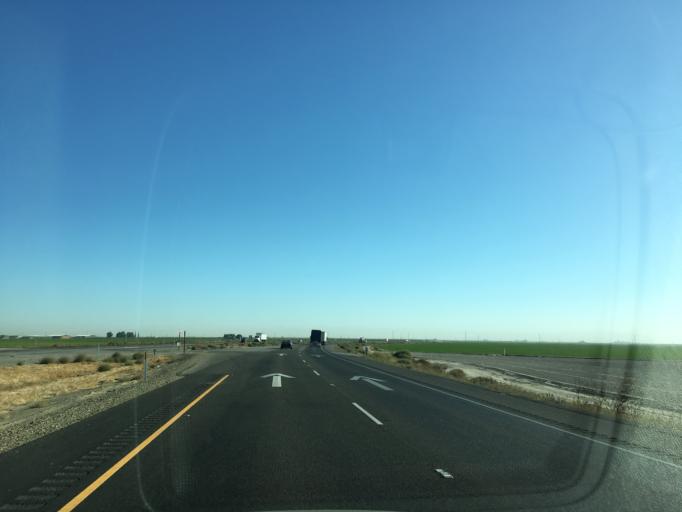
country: US
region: California
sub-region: Merced County
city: Dos Palos
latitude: 37.0651
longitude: -120.5400
